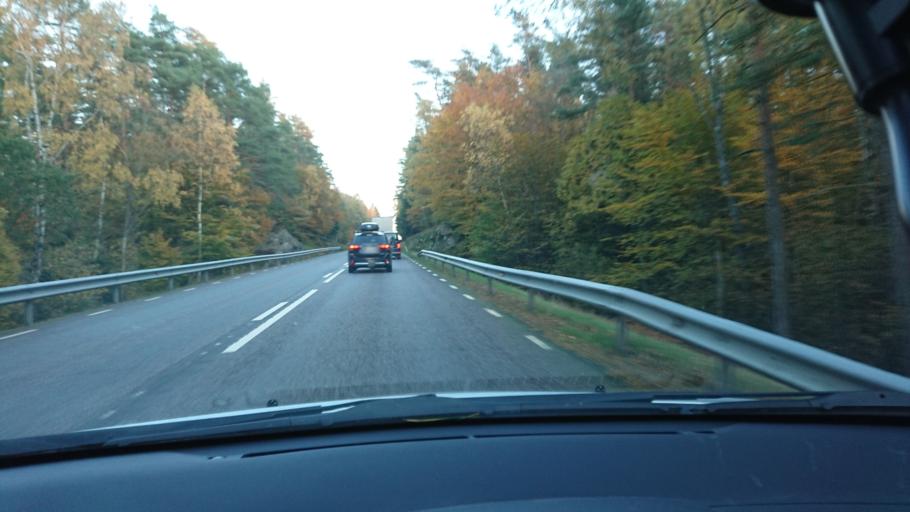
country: SE
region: Halland
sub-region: Laholms Kommun
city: Veinge
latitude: 56.7197
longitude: 13.1759
